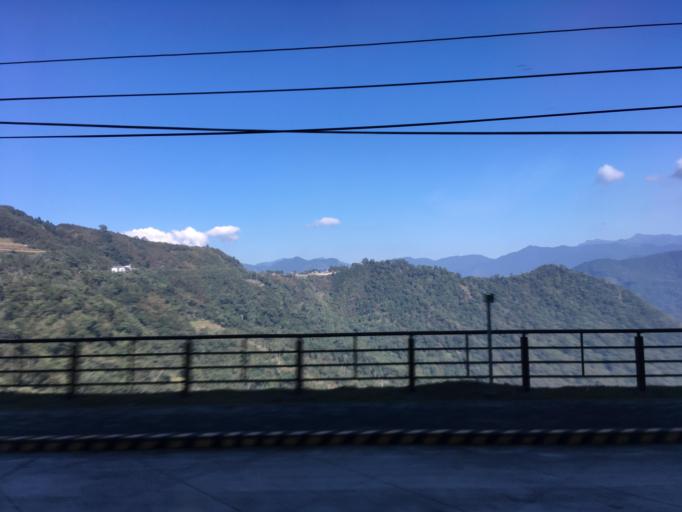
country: TW
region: Taiwan
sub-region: Chiayi
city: Jiayi Shi
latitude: 23.4135
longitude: 120.6518
